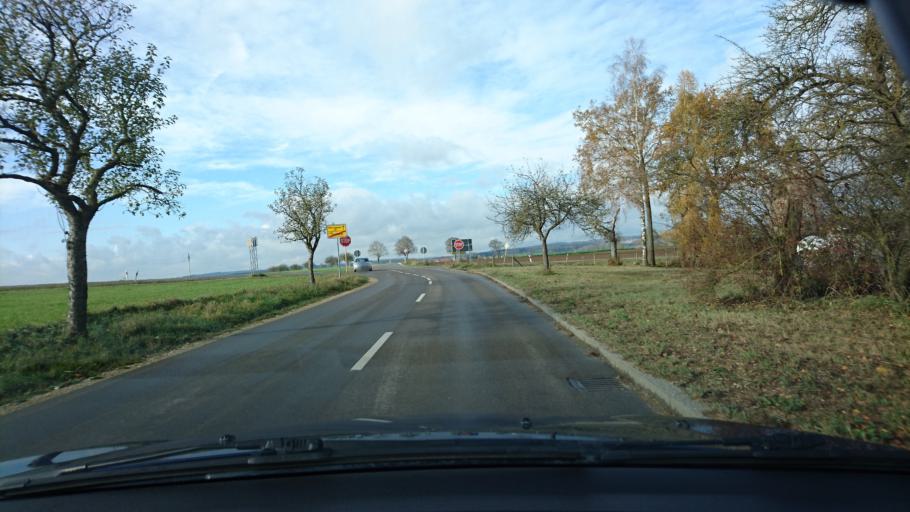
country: DE
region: Bavaria
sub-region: Swabia
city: Hohenaltheim
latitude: 48.7285
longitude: 10.5484
